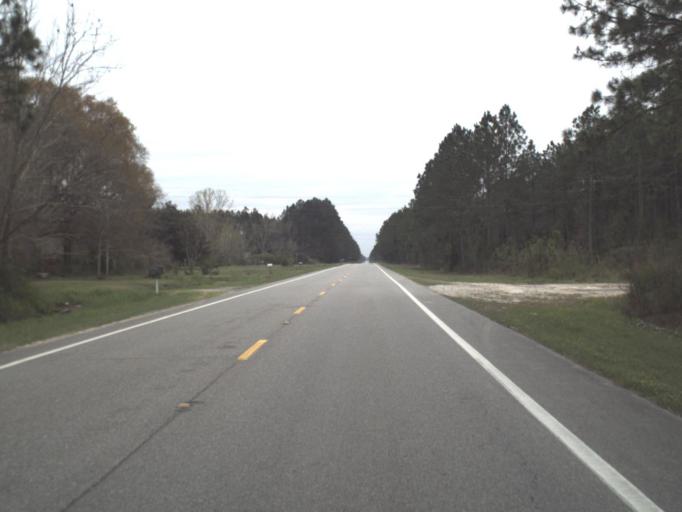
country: US
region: Florida
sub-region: Gulf County
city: Port Saint Joe
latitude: 29.9393
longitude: -85.1883
